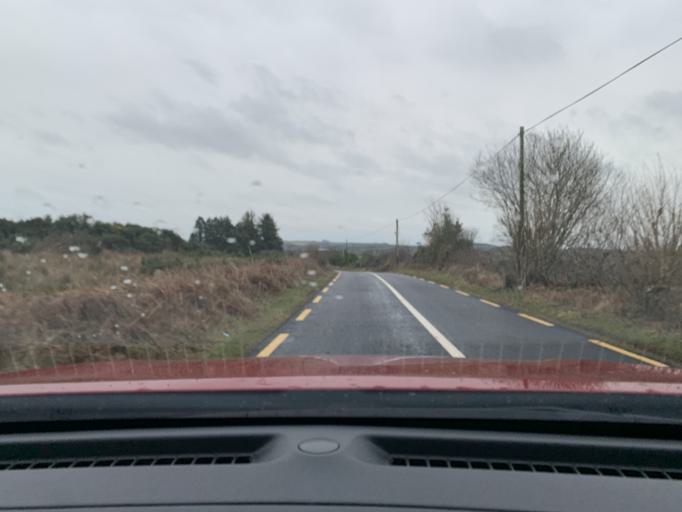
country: IE
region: Connaught
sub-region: Roscommon
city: Boyle
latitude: 53.9796
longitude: -8.3377
